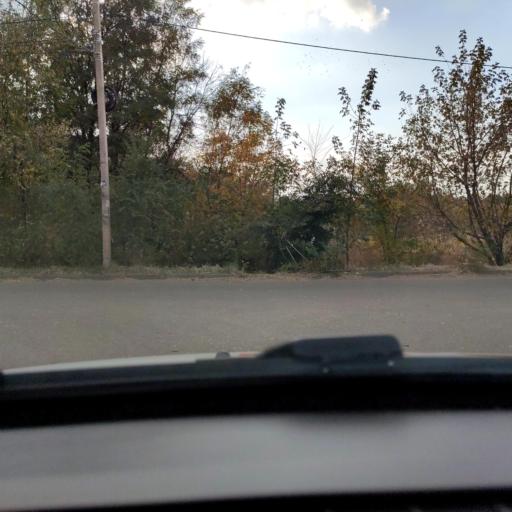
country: RU
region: Voronezj
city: Shilovo
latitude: 51.5609
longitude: 39.1106
